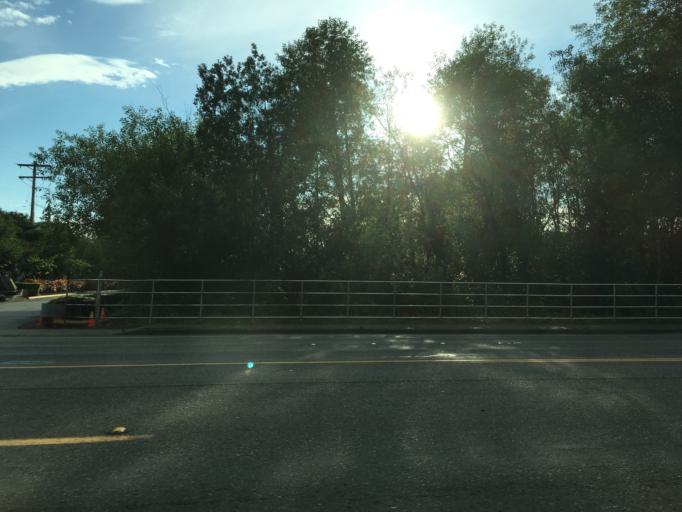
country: US
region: Washington
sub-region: Snohomish County
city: North Creek
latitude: 47.8132
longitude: -122.2075
